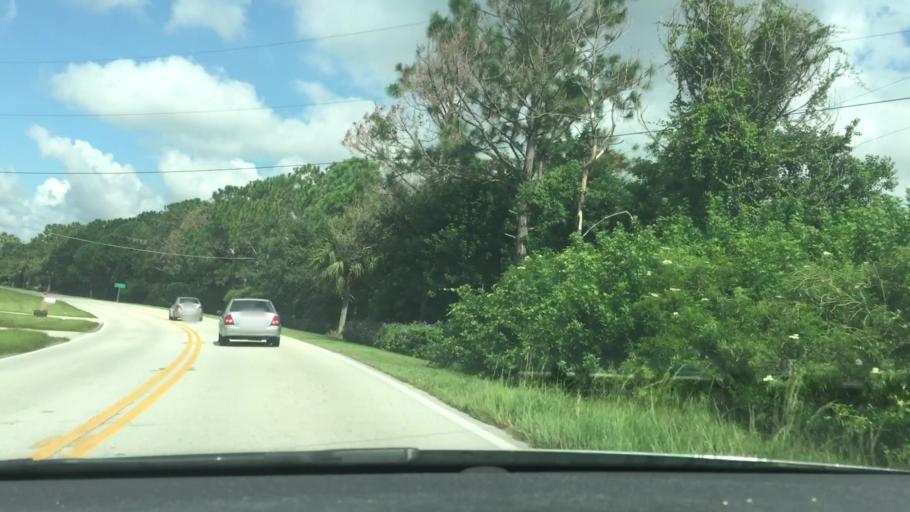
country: US
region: Florida
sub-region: Osceola County
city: Buenaventura Lakes
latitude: 28.3041
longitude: -81.3237
